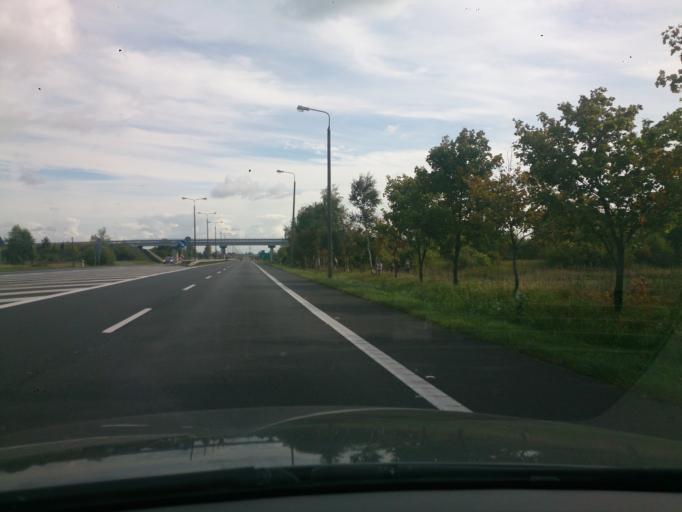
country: PL
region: Kujawsko-Pomorskie
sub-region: Powiat swiecki
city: Swiecie
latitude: 53.4203
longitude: 18.4656
